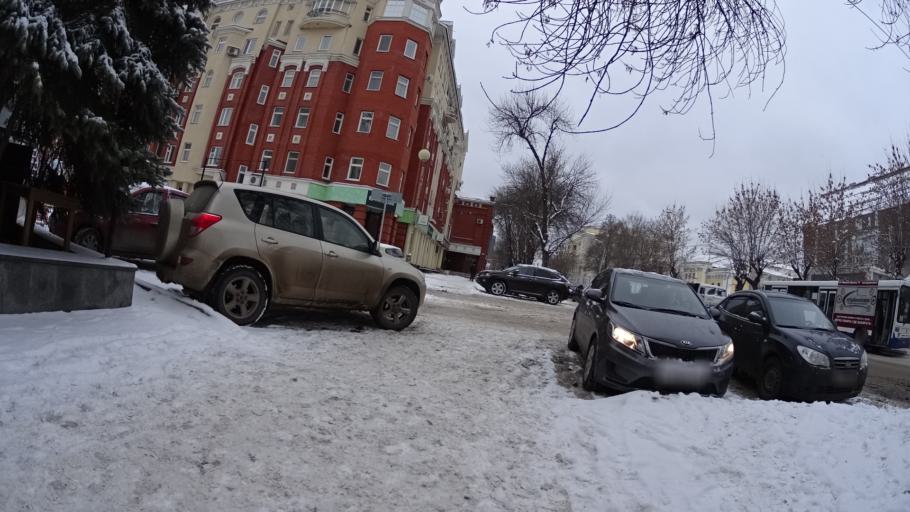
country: RU
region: Bashkortostan
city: Ufa
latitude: 54.7249
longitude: 55.9375
